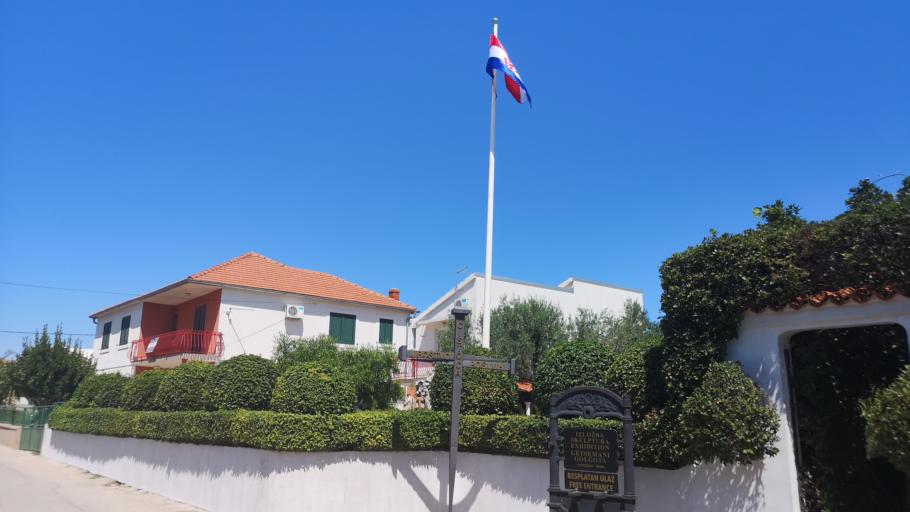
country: HR
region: Sibensko-Kniniska
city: Vodice
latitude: 43.7593
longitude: 15.7717
